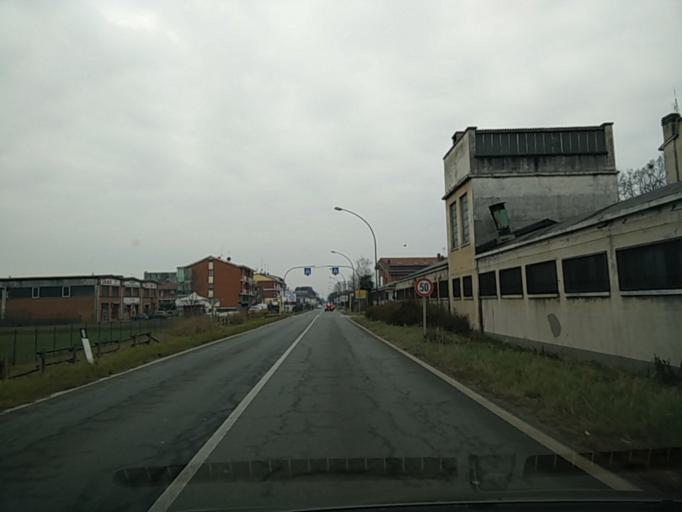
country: IT
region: Piedmont
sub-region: Provincia di Torino
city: Leini
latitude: 45.1980
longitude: 7.7240
